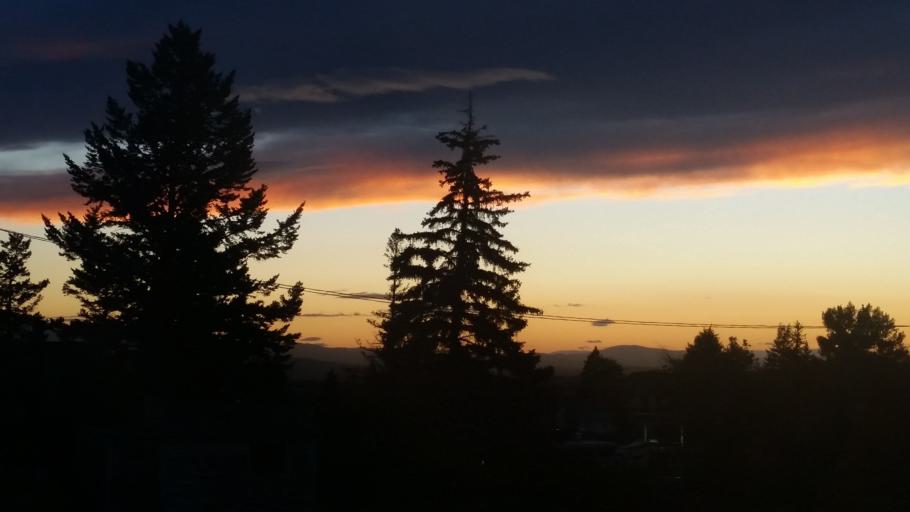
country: US
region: Montana
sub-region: Meagher County
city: White Sulphur Springs
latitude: 46.5478
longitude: -110.8971
